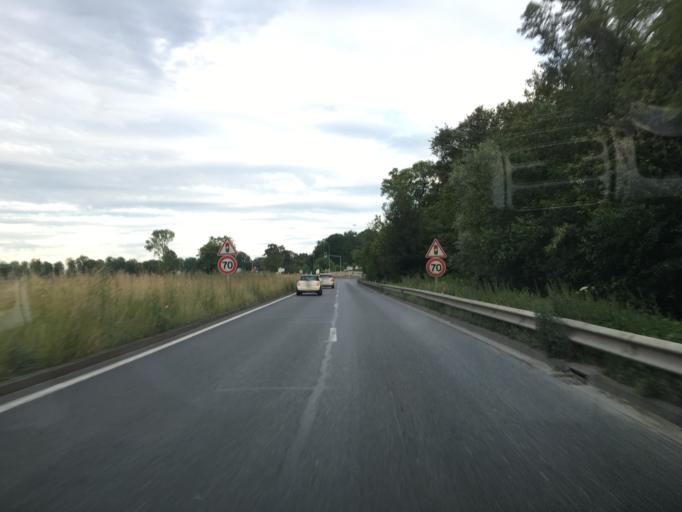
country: FR
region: Ile-de-France
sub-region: Departement du Val-de-Marne
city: Boissy-Saint-Leger
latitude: 48.7359
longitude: 2.5189
